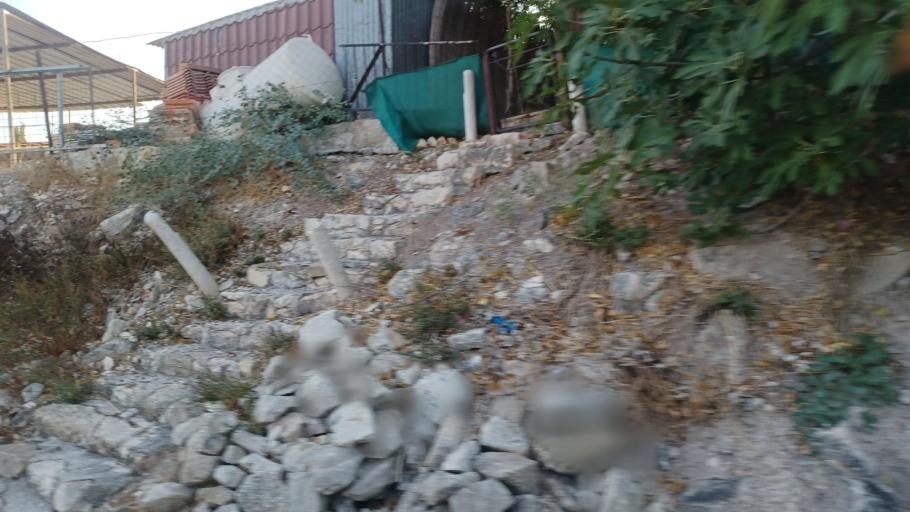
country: CY
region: Pafos
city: Polis
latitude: 34.9681
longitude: 32.4234
